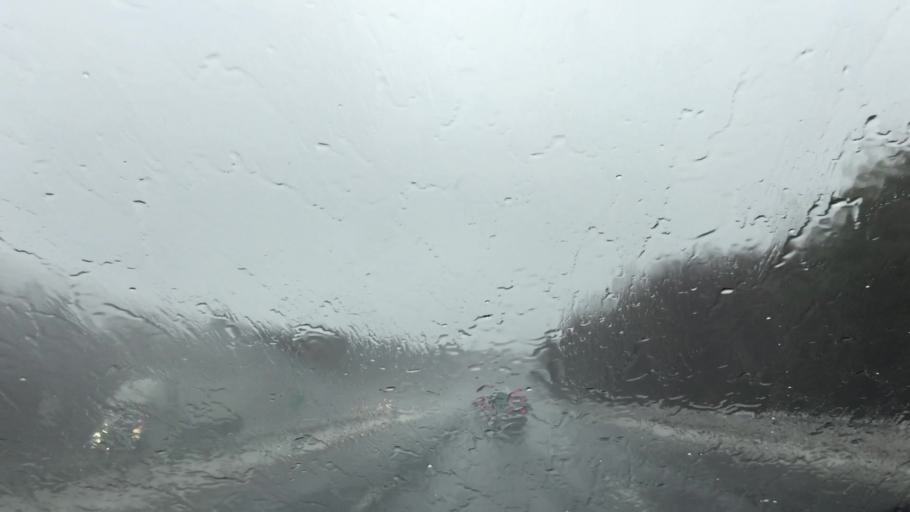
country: US
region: Massachusetts
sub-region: Hampden County
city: Granville
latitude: 42.1720
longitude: -72.9026
